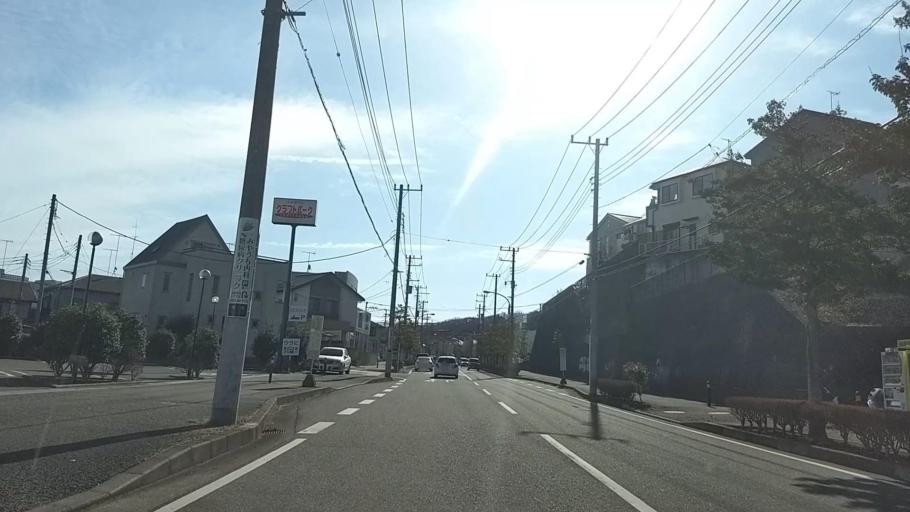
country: JP
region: Kanagawa
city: Hadano
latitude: 35.3633
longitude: 139.2268
